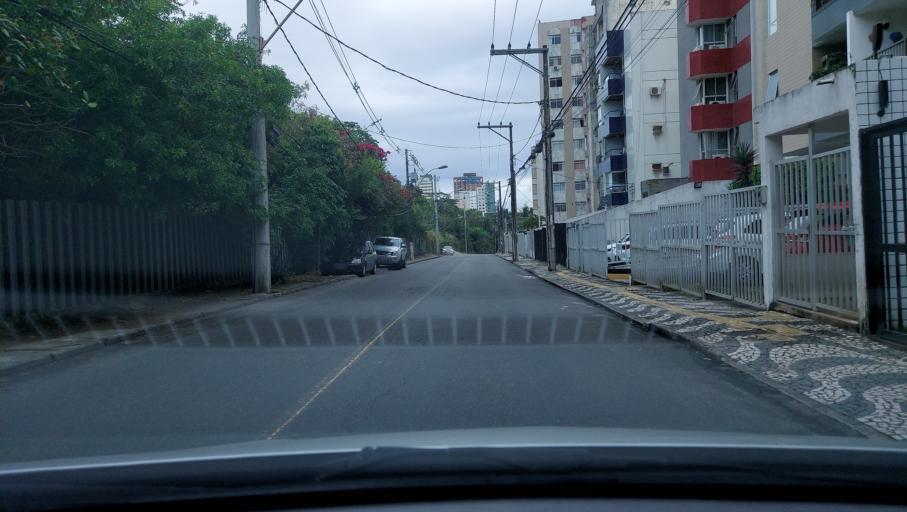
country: BR
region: Bahia
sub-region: Salvador
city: Salvador
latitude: -12.9863
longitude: -38.4434
